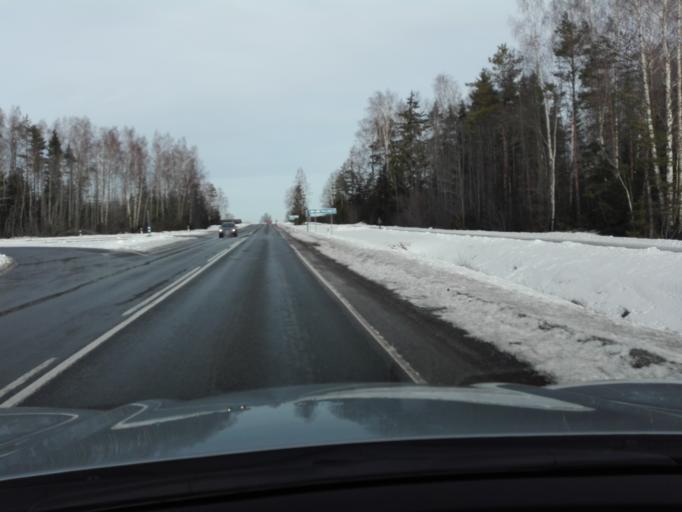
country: EE
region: Raplamaa
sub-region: Rapla vald
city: Rapla
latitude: 58.9895
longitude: 24.7849
